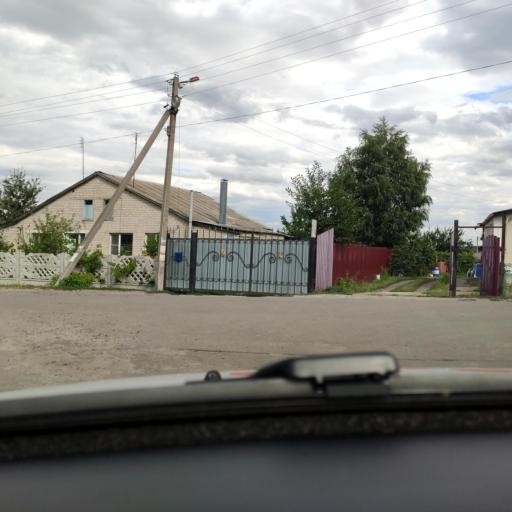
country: RU
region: Voronezj
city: Orlovo
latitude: 51.6546
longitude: 39.5723
